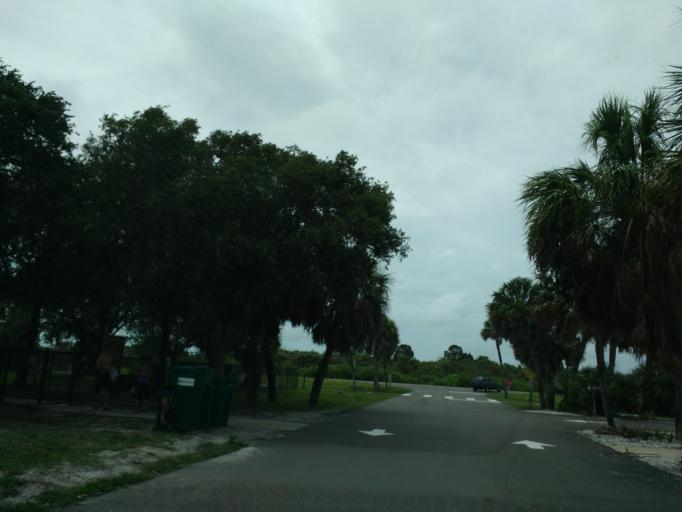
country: US
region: Florida
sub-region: Pinellas County
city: Tierra Verde
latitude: 27.6168
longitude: -82.7275
